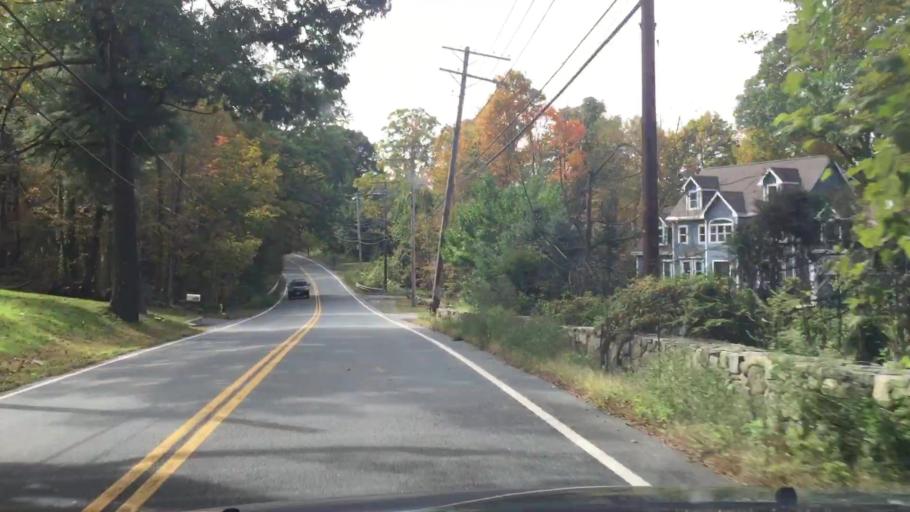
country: US
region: Massachusetts
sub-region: Middlesex County
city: Tewksbury
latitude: 42.6716
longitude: -71.2303
